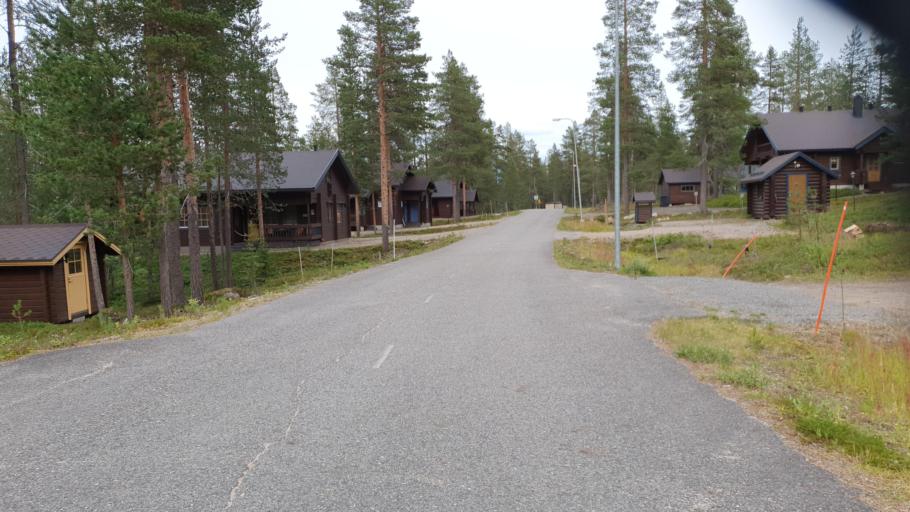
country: FI
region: Lapland
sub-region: Tunturi-Lappi
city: Kolari
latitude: 67.5926
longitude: 24.1529
